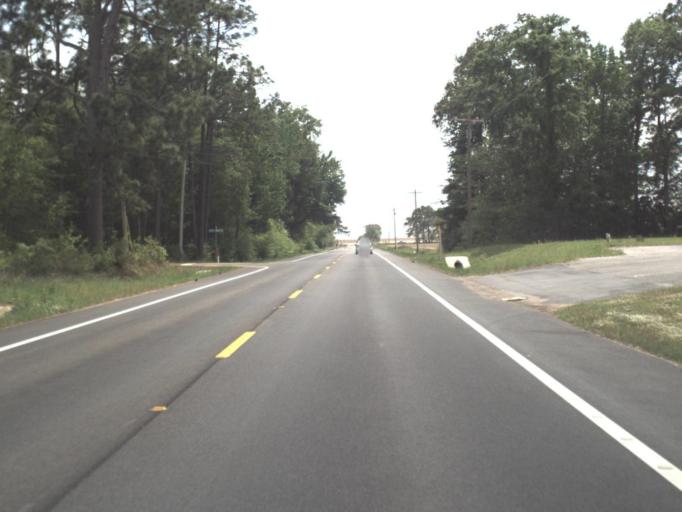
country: US
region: Florida
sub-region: Escambia County
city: Century
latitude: 30.9182
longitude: -87.1639
